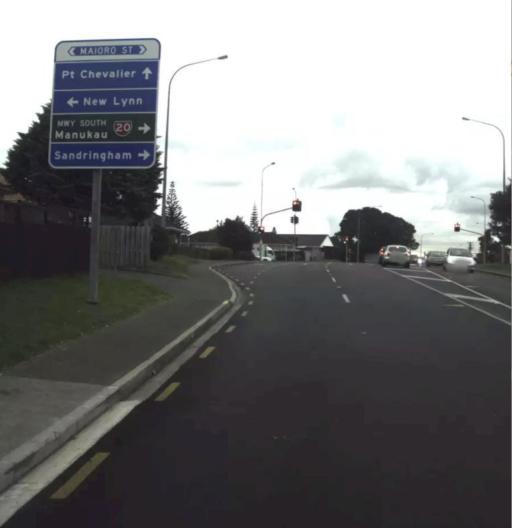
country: NZ
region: Auckland
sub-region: Auckland
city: Auckland
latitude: -36.9060
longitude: 174.7218
